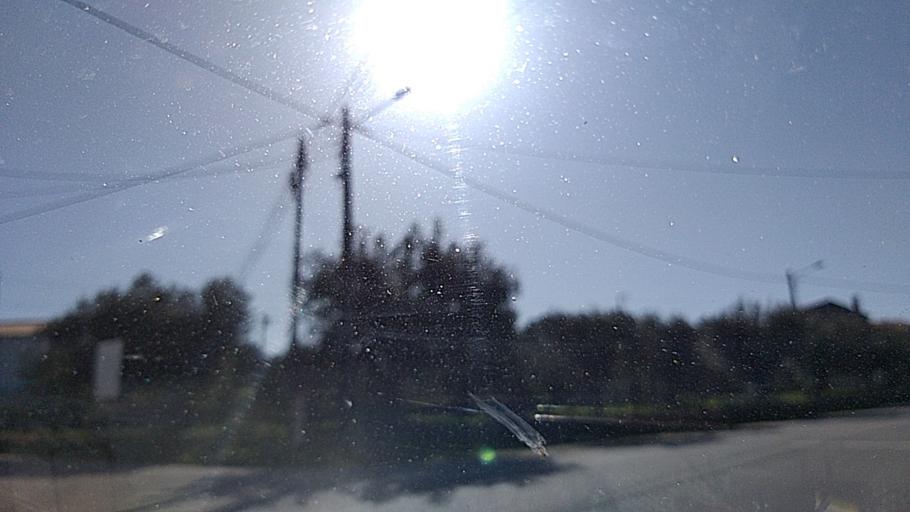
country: PT
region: Guarda
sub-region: Celorico da Beira
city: Celorico da Beira
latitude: 40.6677
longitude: -7.3811
